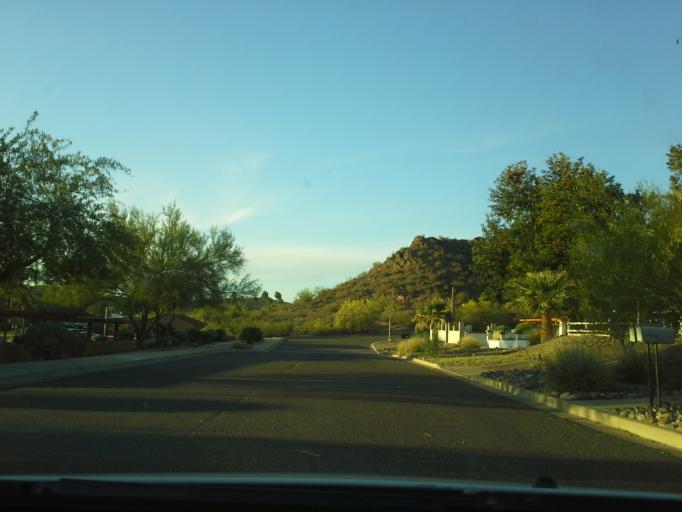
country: US
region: Arizona
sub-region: Maricopa County
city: Paradise Valley
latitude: 33.5767
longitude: -112.0479
